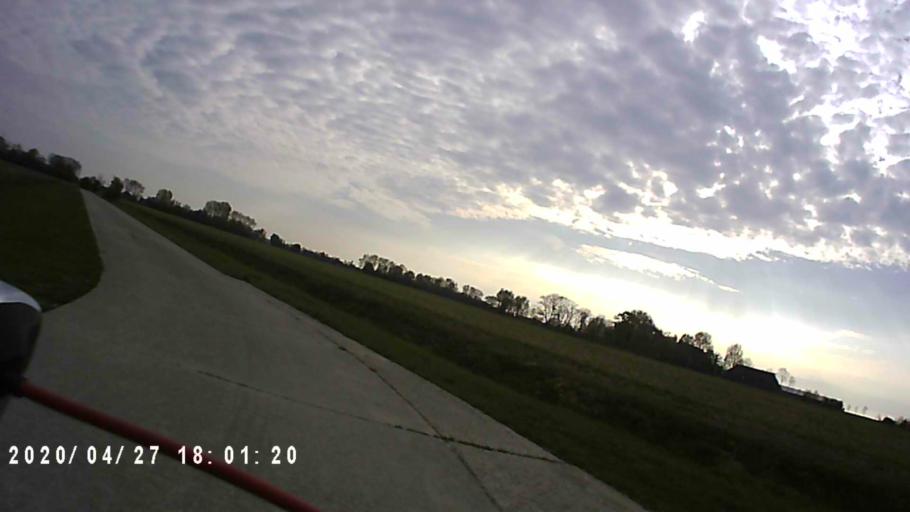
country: NL
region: Groningen
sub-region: Gemeente Winsum
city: Winsum
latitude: 53.4065
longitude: 6.4521
